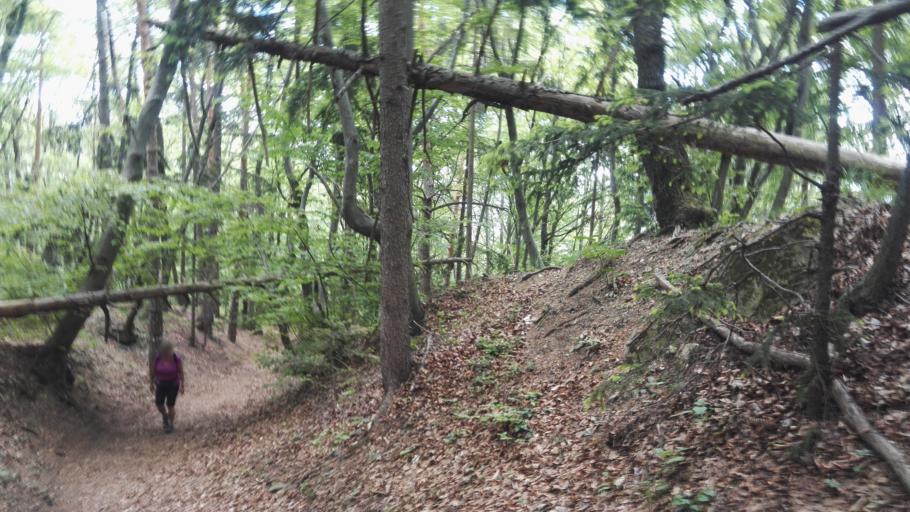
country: AT
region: Styria
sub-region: Graz Stadt
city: Goesting
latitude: 47.0866
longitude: 15.3908
